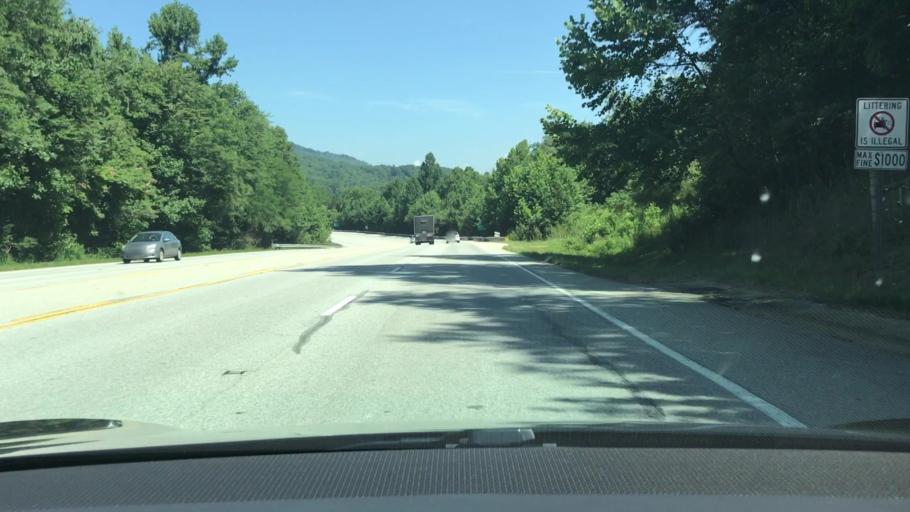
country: US
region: Georgia
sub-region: Rabun County
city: Mountain City
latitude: 35.0056
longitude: -83.3836
